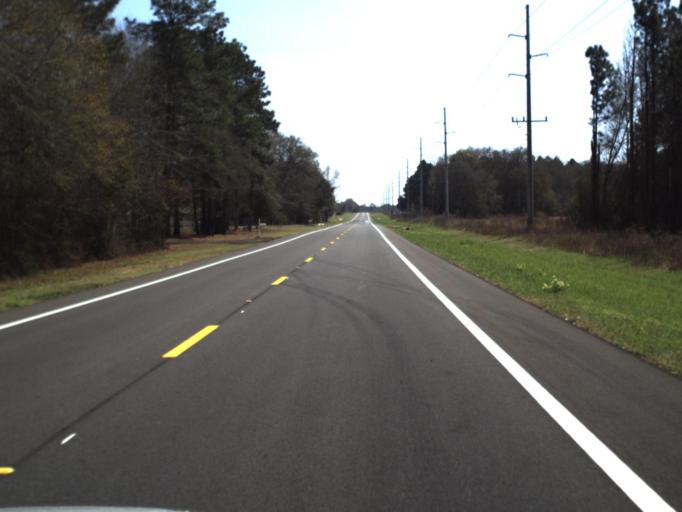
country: US
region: Florida
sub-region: Jackson County
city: Sneads
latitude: 30.7973
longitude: -85.0287
